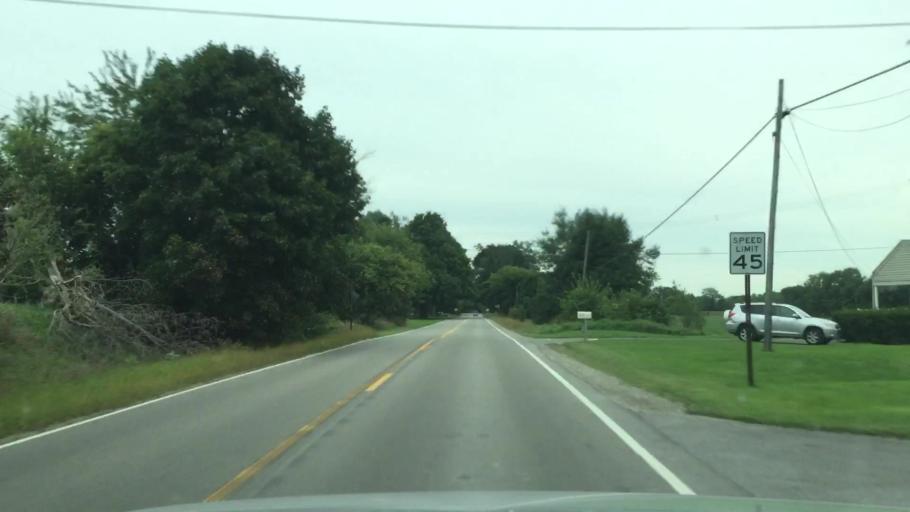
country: US
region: Michigan
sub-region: Washtenaw County
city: Ypsilanti
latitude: 42.1732
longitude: -83.6436
